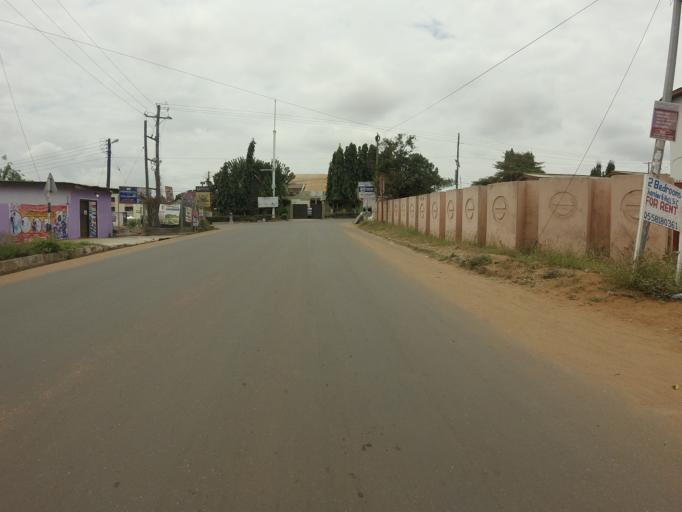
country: GH
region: Greater Accra
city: Nungua
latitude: 5.6074
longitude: -0.0941
